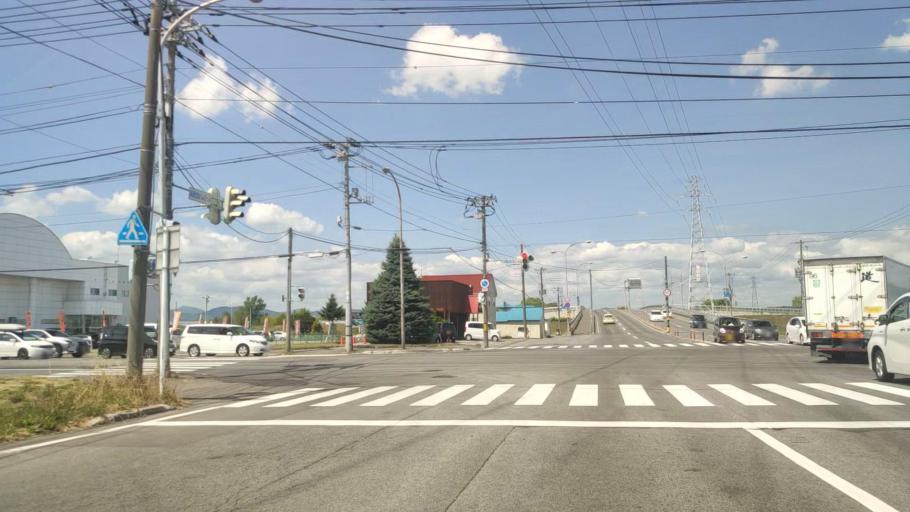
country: JP
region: Hokkaido
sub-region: Asahikawa-shi
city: Asahikawa
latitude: 43.7952
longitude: 142.3991
